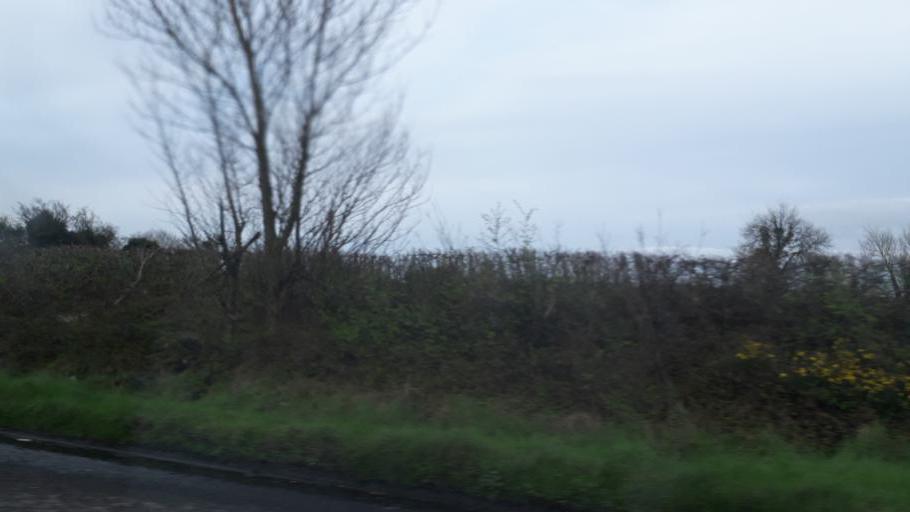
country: IE
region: Leinster
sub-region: Laois
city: Portlaoise
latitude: 53.0082
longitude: -7.3046
